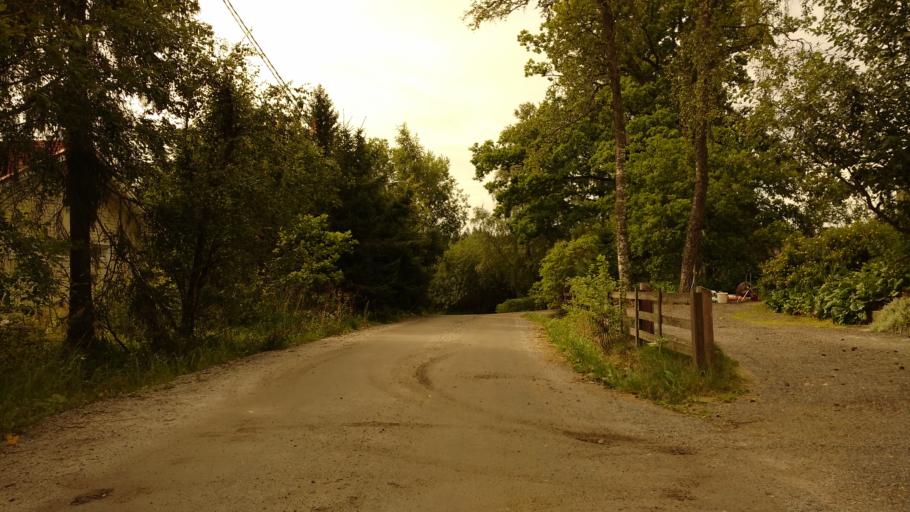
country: FI
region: Varsinais-Suomi
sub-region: Turku
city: Kaarina
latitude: 60.4448
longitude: 22.4219
